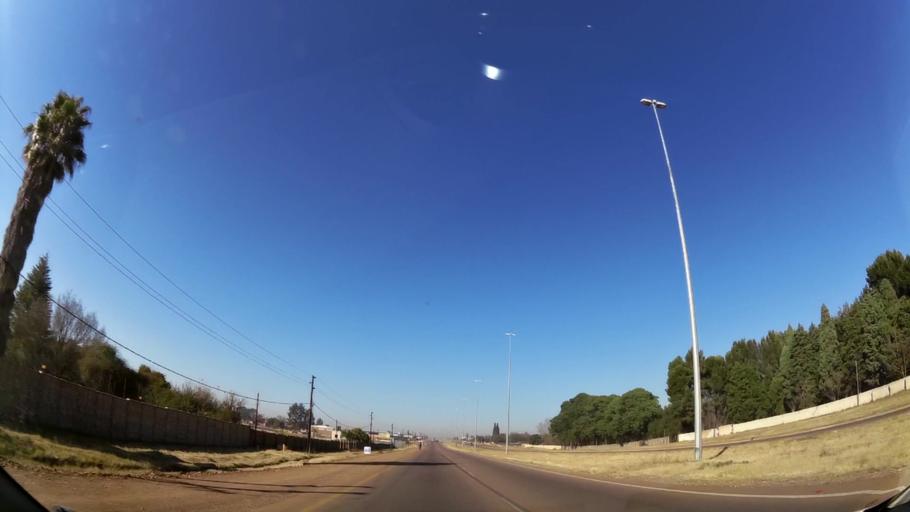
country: ZA
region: Gauteng
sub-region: City of Tshwane Metropolitan Municipality
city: Centurion
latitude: -25.8536
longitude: 28.1085
